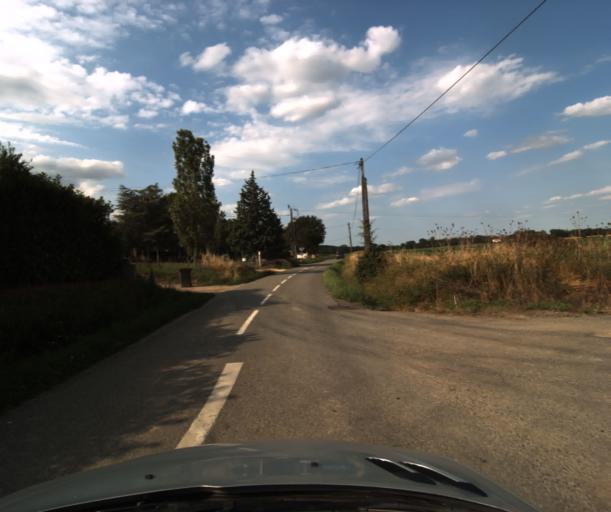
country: FR
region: Midi-Pyrenees
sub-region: Departement de la Haute-Garonne
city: Fonsorbes
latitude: 43.5116
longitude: 1.2204
